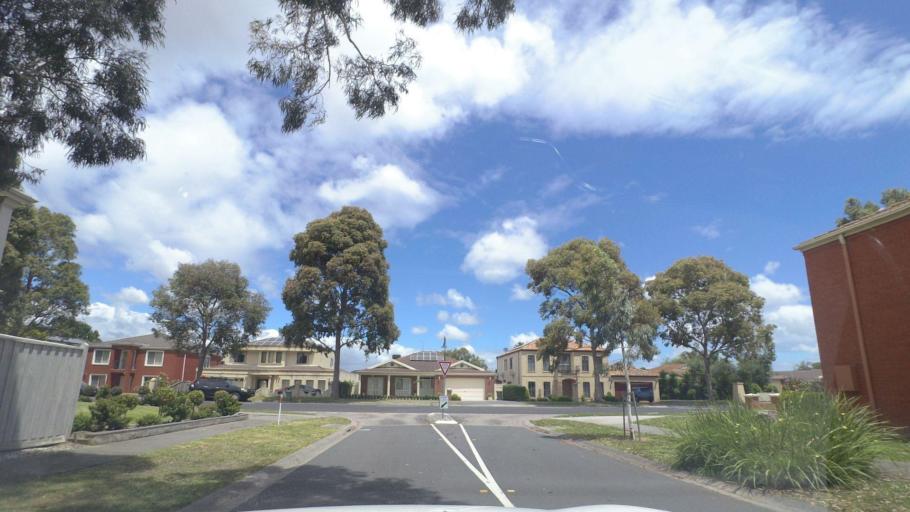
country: AU
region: Victoria
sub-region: Knox
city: Knoxfield
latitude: -37.9056
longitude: 145.2673
